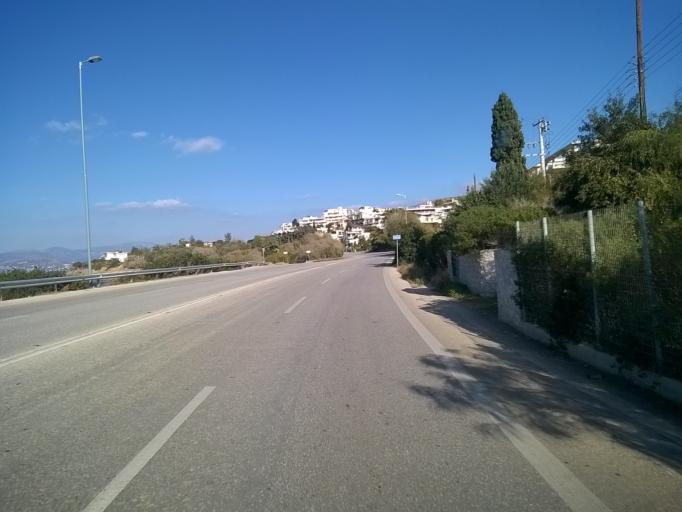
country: GR
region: Attica
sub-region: Nomarchia Anatolikis Attikis
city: Saronida
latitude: 37.7409
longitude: 23.9048
